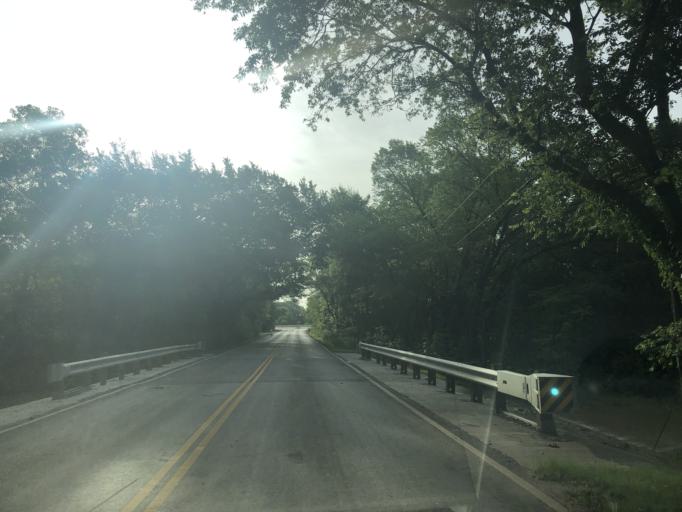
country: US
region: Texas
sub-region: Dallas County
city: Grand Prairie
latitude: 32.7924
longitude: -96.9975
